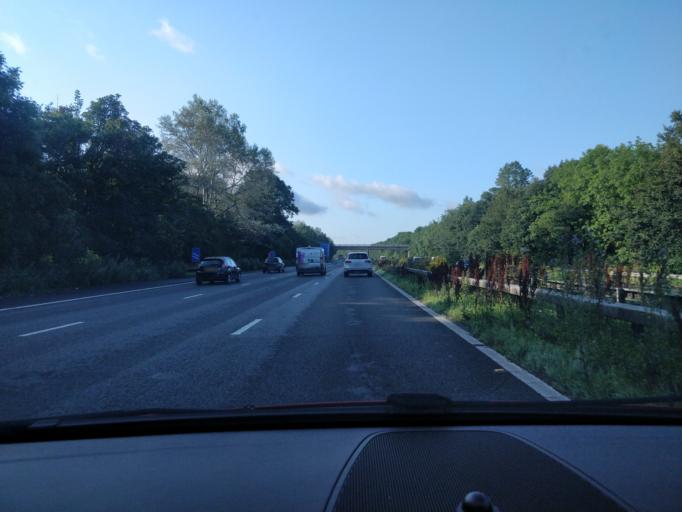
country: GB
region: England
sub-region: Knowsley
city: Knowsley
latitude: 53.4432
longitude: -2.8588
